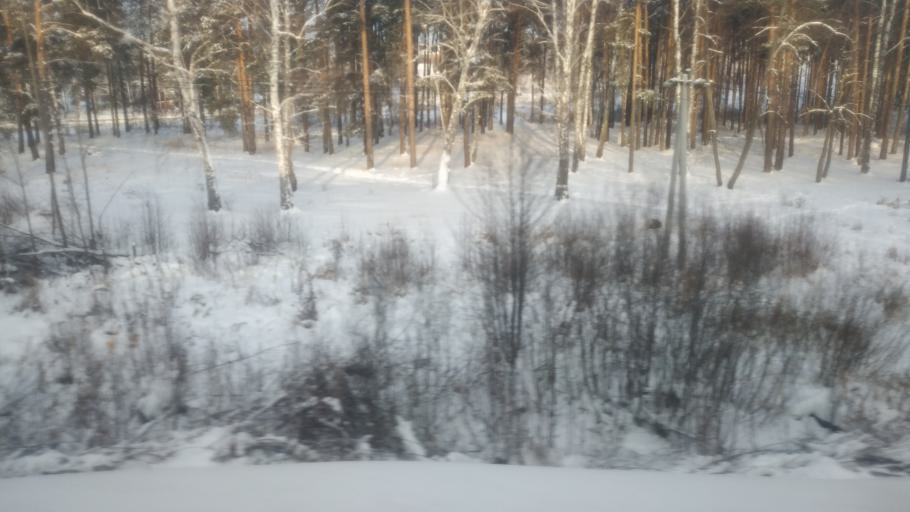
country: RU
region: Kirov
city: Krasnaya Polyana
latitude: 56.2511
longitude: 51.1469
